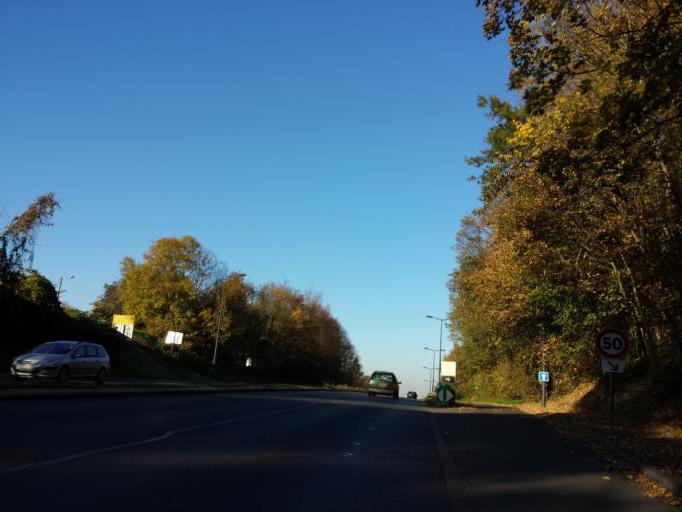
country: FR
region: Ile-de-France
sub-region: Departement du Val-d'Oise
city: Ecouen
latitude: 49.0138
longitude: 2.3852
